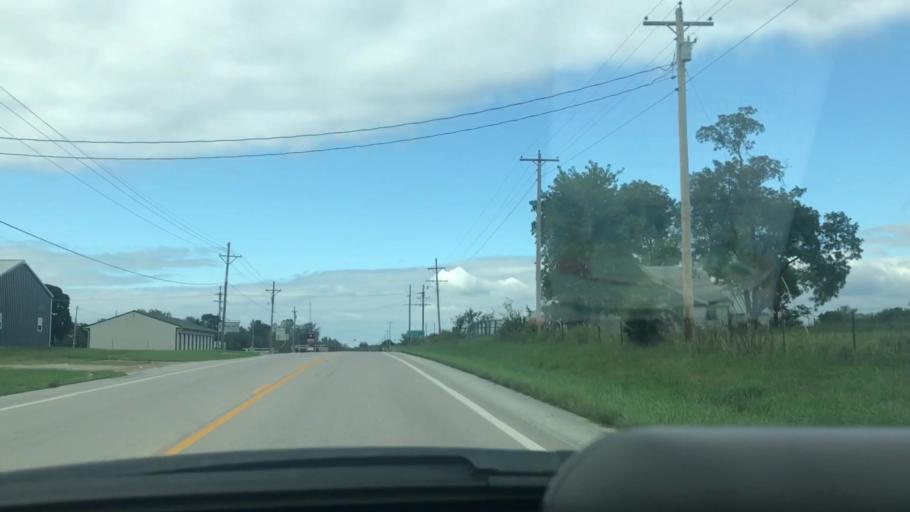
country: US
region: Missouri
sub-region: Hickory County
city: Hermitage
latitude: 37.9384
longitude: -93.2082
